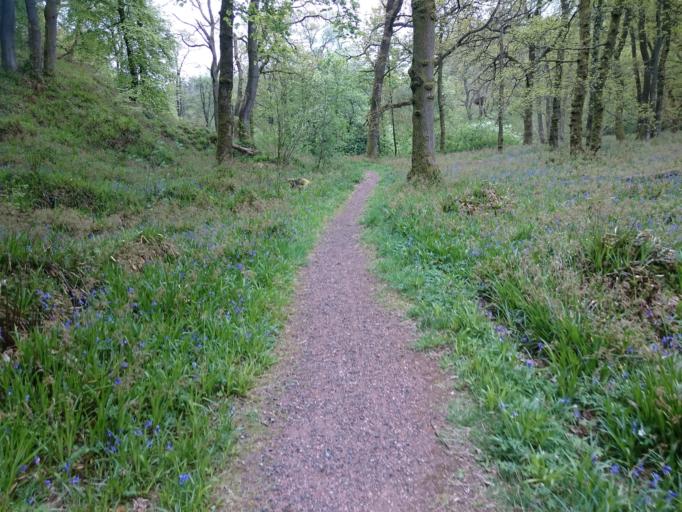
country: GB
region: Scotland
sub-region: Falkirk
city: Dunipace
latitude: 56.0277
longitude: -3.9490
